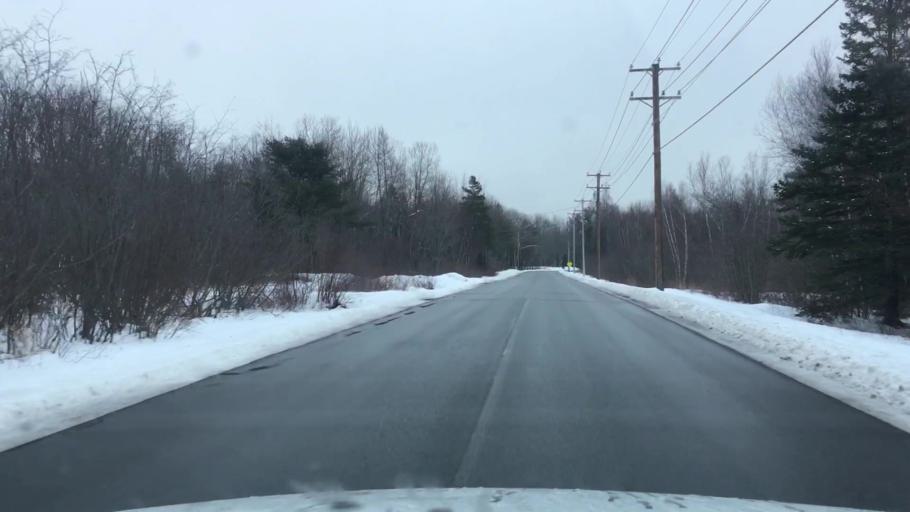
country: US
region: Maine
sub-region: Hancock County
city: Trenton
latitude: 44.4078
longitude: -68.3253
